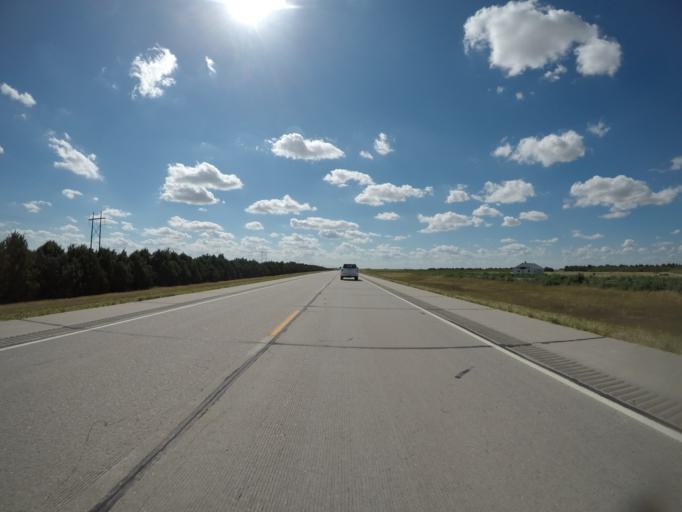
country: US
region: Colorado
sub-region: Phillips County
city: Holyoke
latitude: 40.5985
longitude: -102.3888
